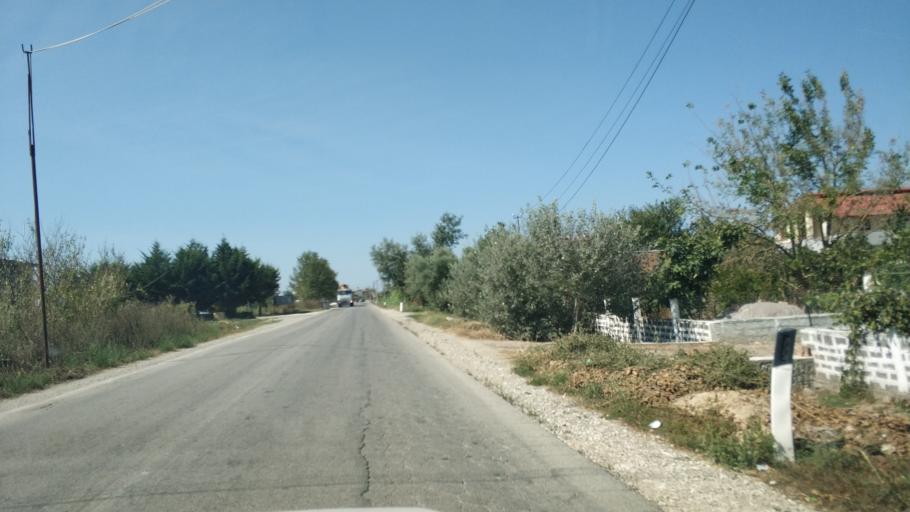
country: AL
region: Fier
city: Terbuf
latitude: 41.0520
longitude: 19.5875
